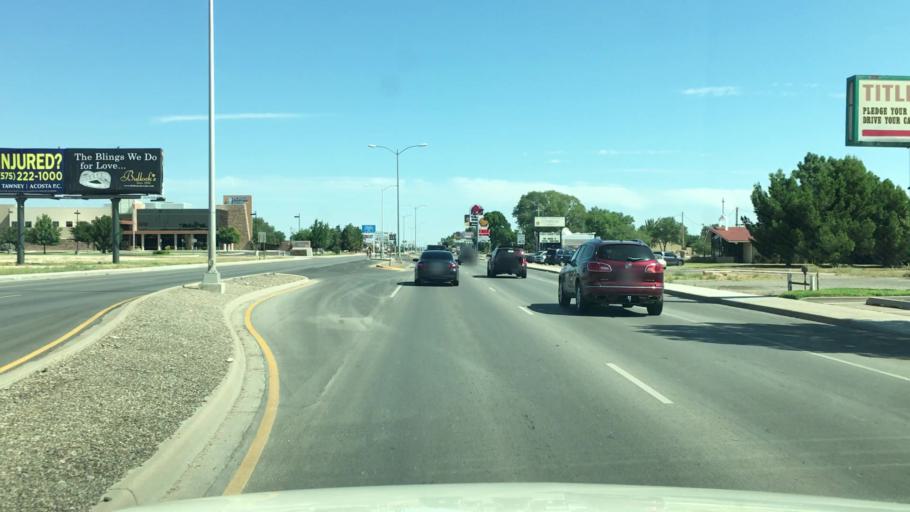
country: US
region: New Mexico
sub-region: Chaves County
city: Roswell
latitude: 33.4310
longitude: -104.5231
